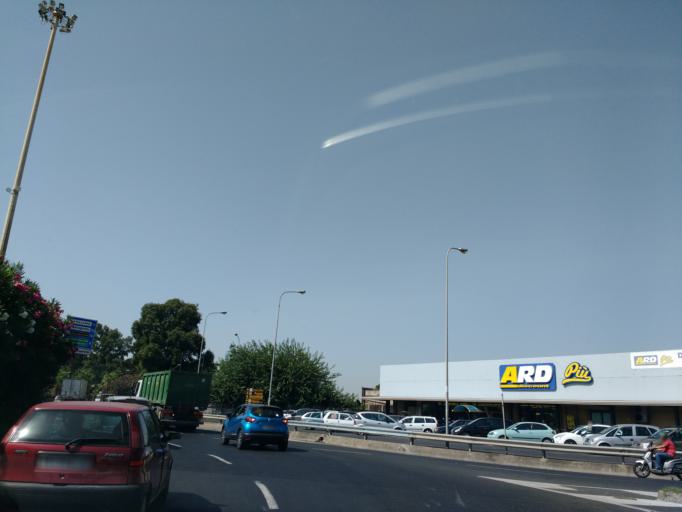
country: IT
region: Sicily
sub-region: Catania
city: Catania
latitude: 37.4889
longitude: 15.0827
